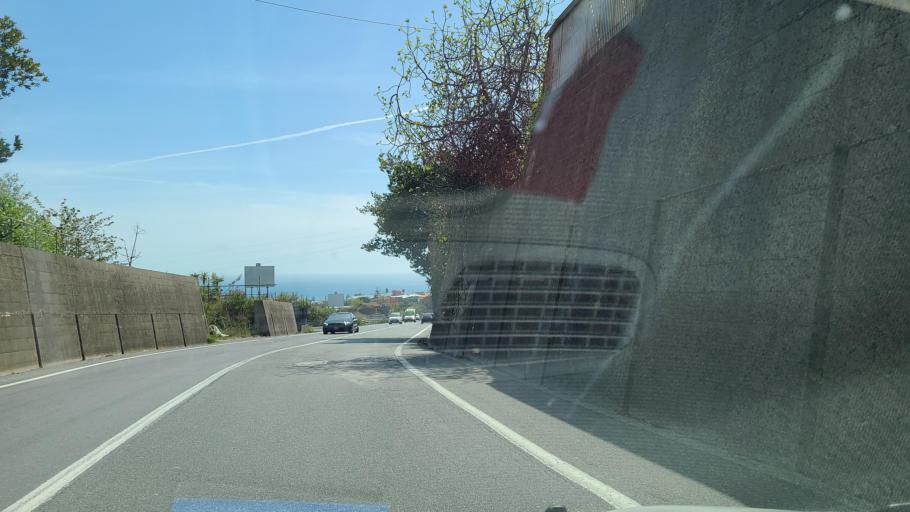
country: IT
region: Liguria
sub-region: Provincia di Imperia
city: Taggia
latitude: 43.8455
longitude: 7.8415
